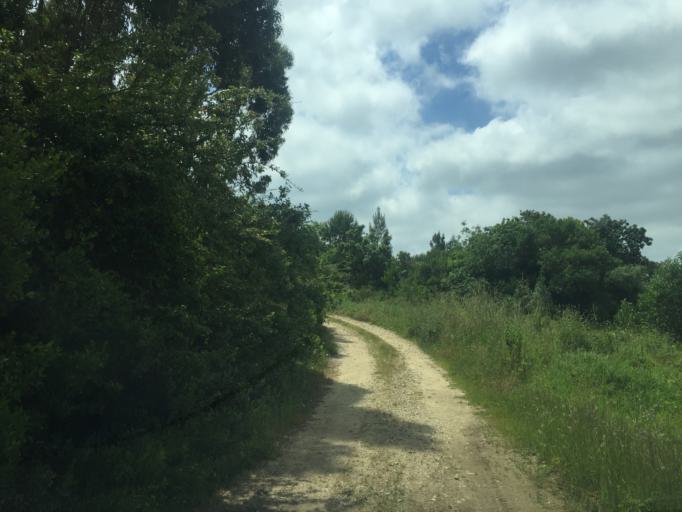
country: PT
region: Coimbra
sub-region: Figueira da Foz
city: Tavarede
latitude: 40.1859
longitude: -8.8230
